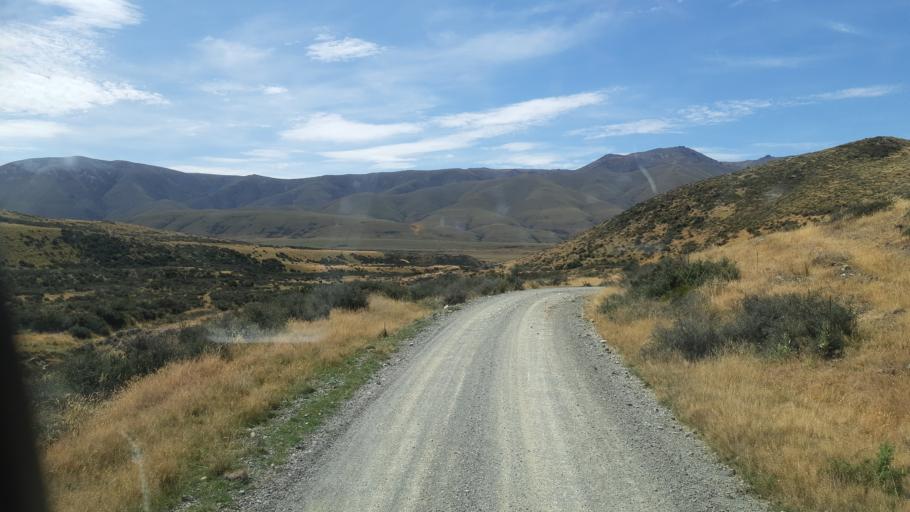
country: NZ
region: Canterbury
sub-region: Timaru District
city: Pleasant Point
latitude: -44.3524
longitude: 170.6204
